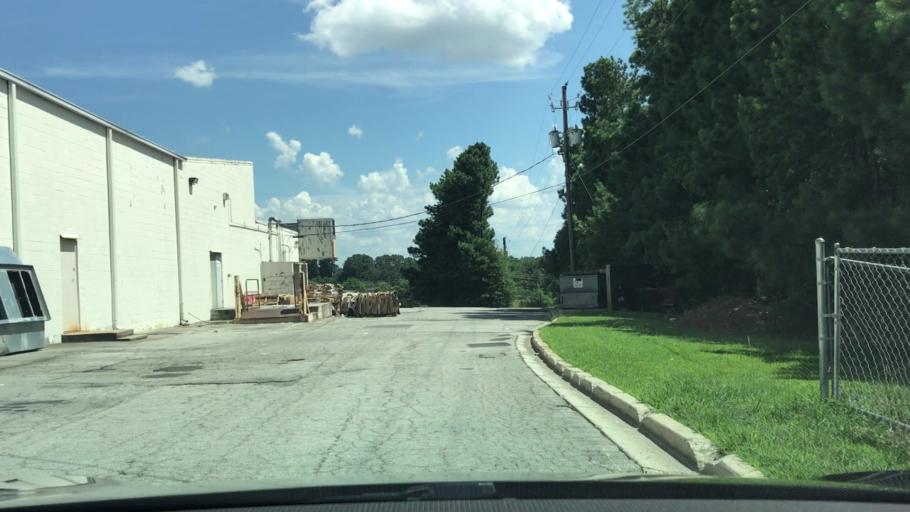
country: US
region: Georgia
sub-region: Gwinnett County
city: Sugar Hill
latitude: 34.0955
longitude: -84.0164
